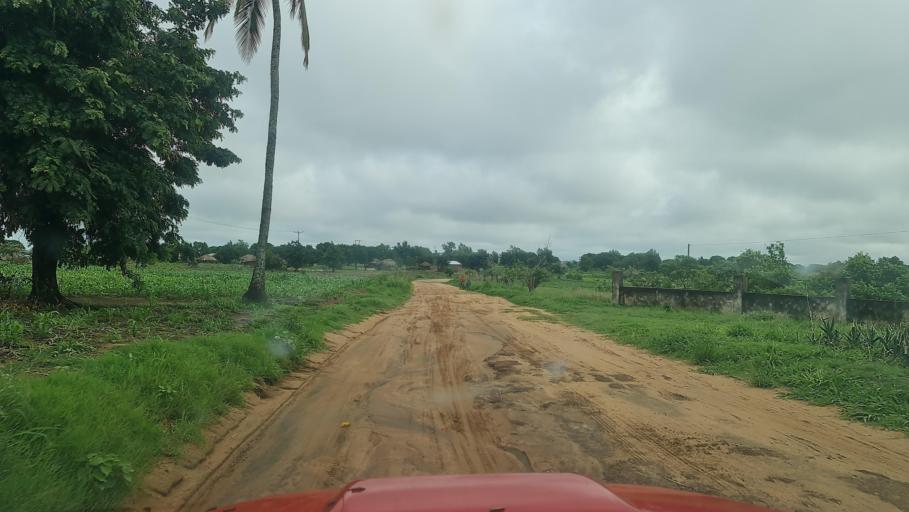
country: MW
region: Southern Region
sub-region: Nsanje District
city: Nsanje
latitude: -17.1946
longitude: 35.7014
